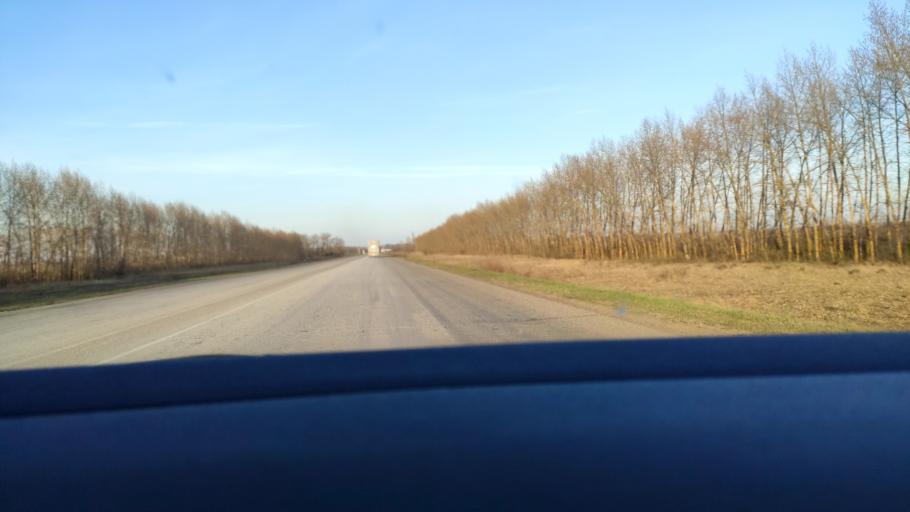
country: RU
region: Voronezj
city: Novovoronezh
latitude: 51.4203
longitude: 39.2881
